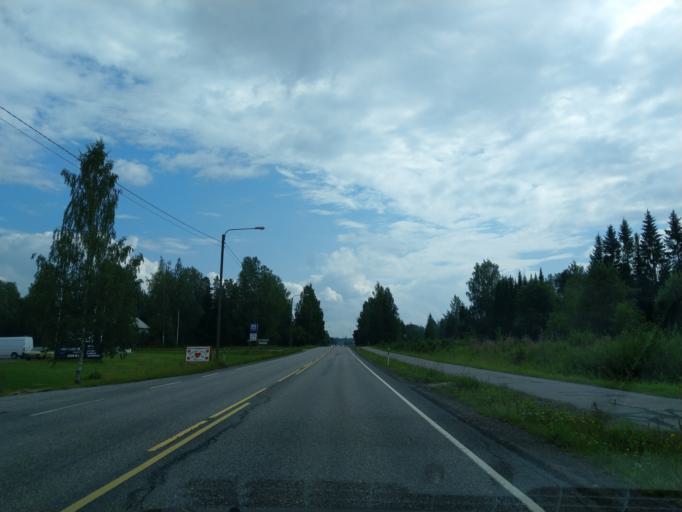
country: FI
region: South Karelia
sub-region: Imatra
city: Parikkala
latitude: 61.5925
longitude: 29.4870
